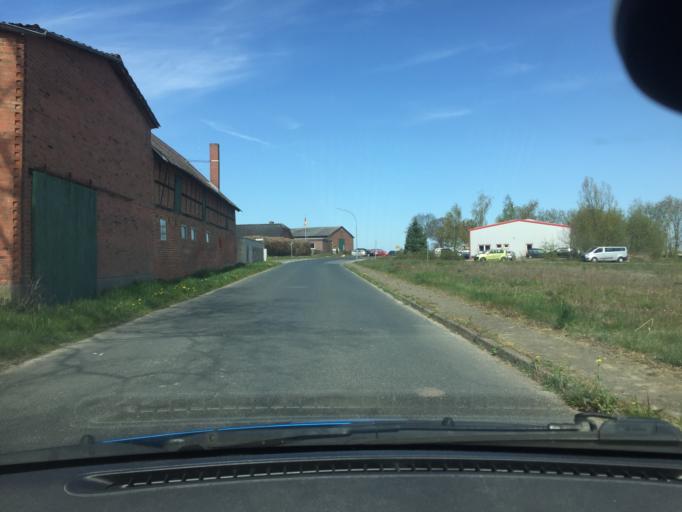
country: DE
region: Lower Saxony
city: Ratzlingen
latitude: 52.9772
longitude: 10.6752
